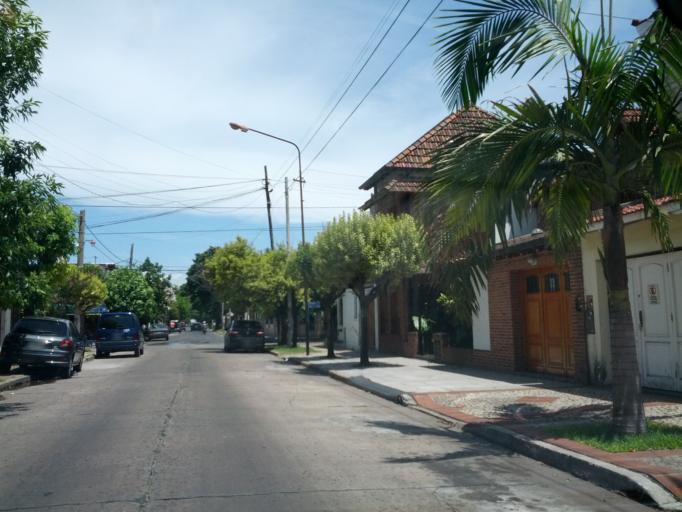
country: AR
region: Buenos Aires
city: San Justo
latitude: -34.6473
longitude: -58.5716
